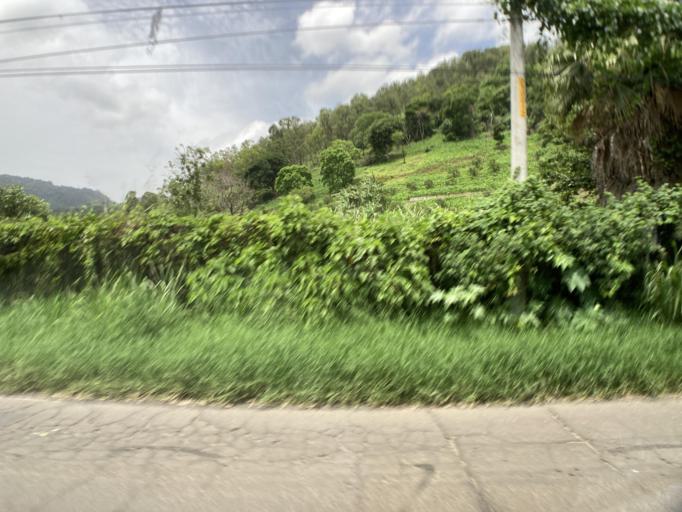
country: GT
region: Guatemala
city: Villa Canales
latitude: 14.4289
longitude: -90.5573
